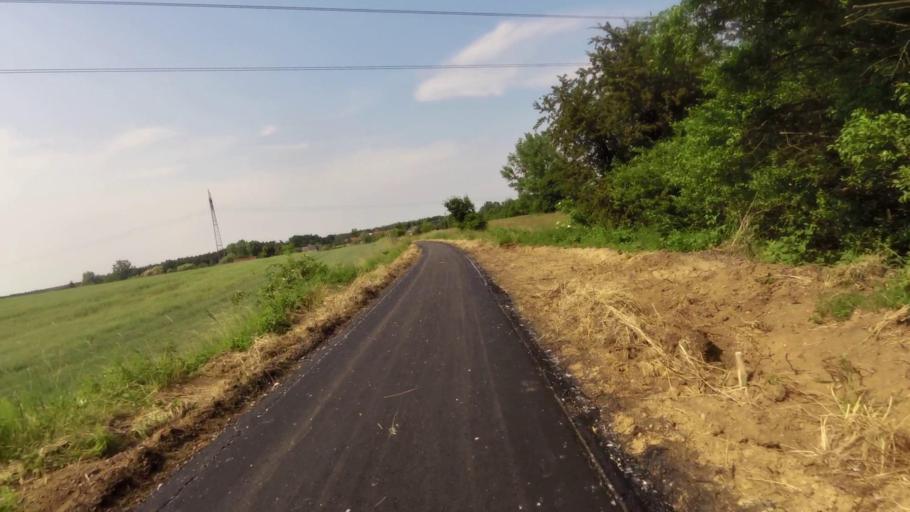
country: PL
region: West Pomeranian Voivodeship
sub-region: Powiat pyrzycki
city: Bielice
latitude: 53.2135
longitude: 14.6117
